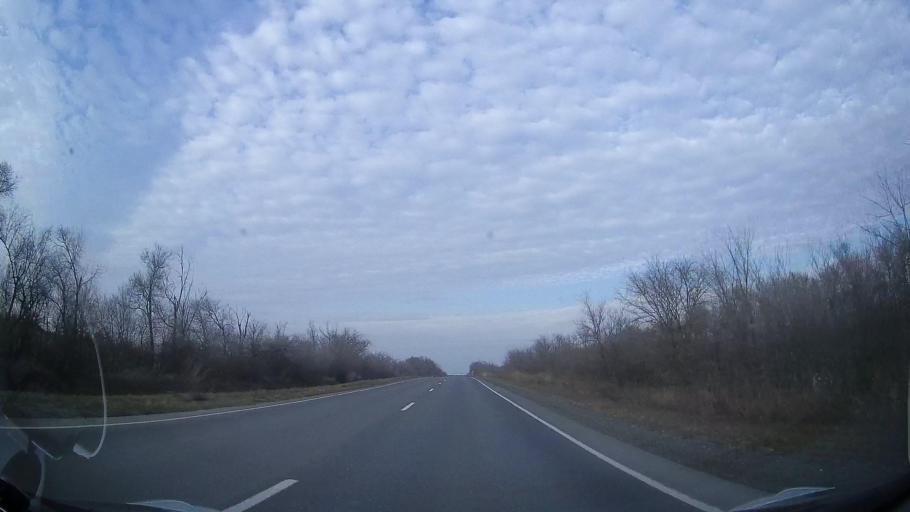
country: RU
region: Rostov
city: Bagayevskaya
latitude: 47.1414
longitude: 40.2766
